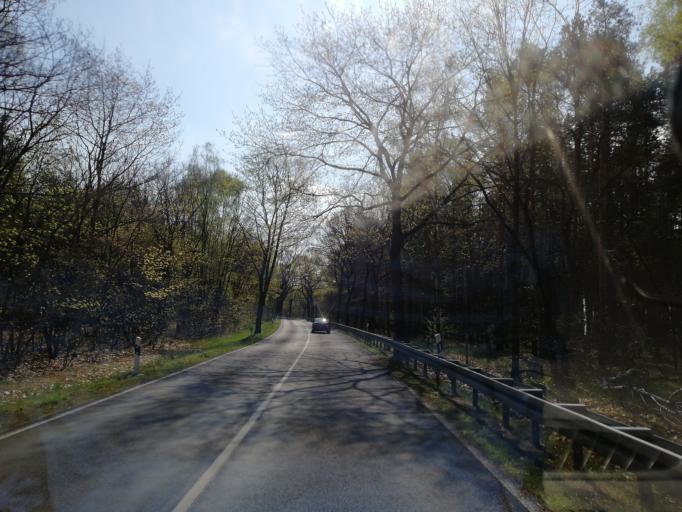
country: DE
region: Brandenburg
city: Calau
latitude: 51.7738
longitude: 13.8951
